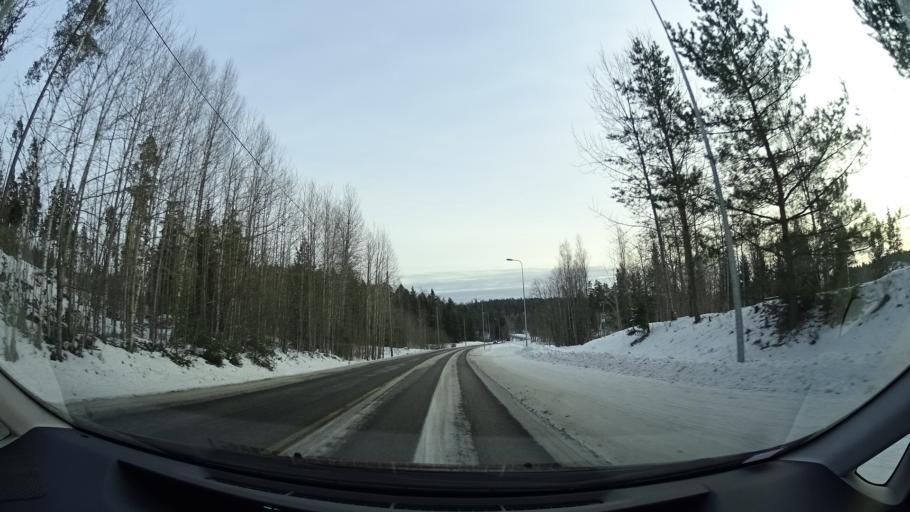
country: FI
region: Uusimaa
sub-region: Helsinki
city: Espoo
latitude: 60.2658
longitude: 24.5980
